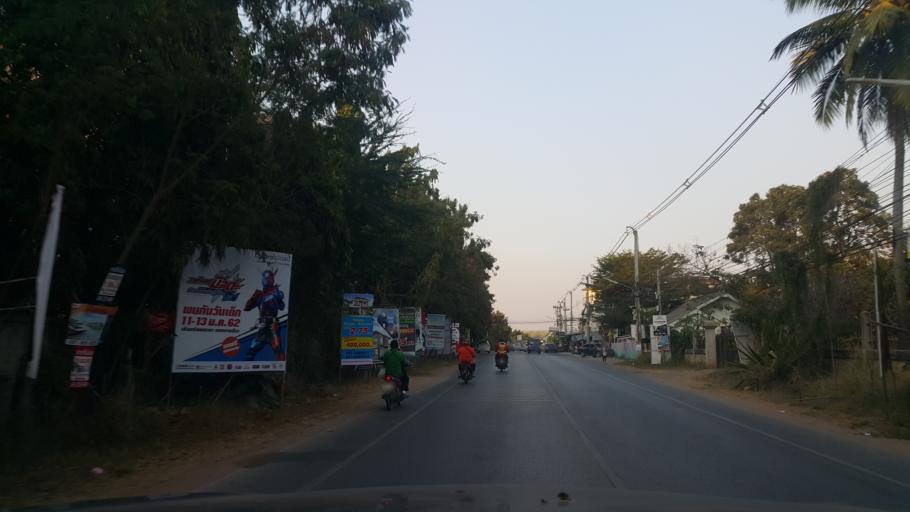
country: TH
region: Nakhon Ratchasima
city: Nakhon Ratchasima
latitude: 14.9464
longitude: 102.0428
